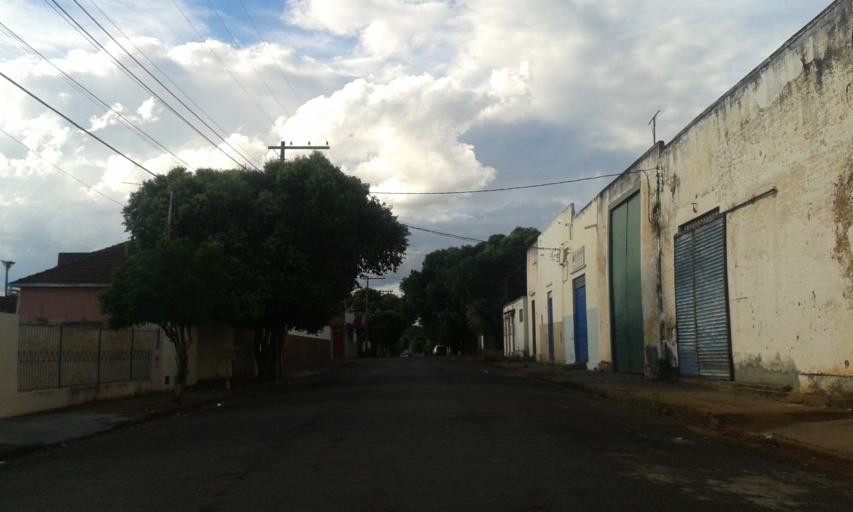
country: BR
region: Minas Gerais
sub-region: Ituiutaba
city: Ituiutaba
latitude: -18.9679
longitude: -49.4585
